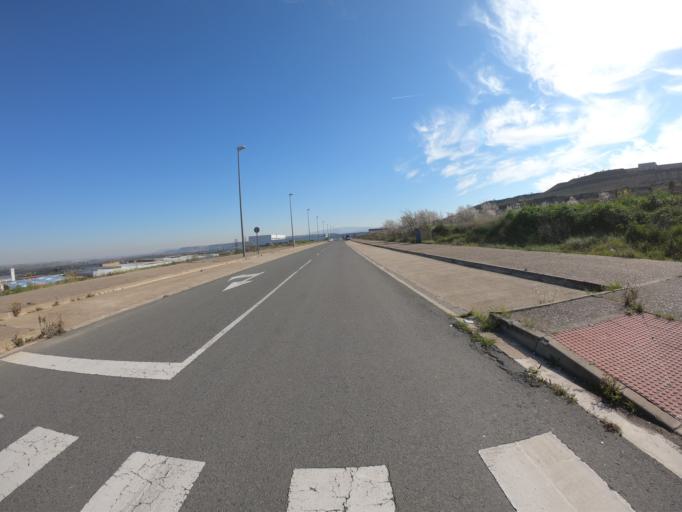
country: ES
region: Basque Country
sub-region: Provincia de Alava
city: Oyon
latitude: 42.4808
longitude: -2.4222
